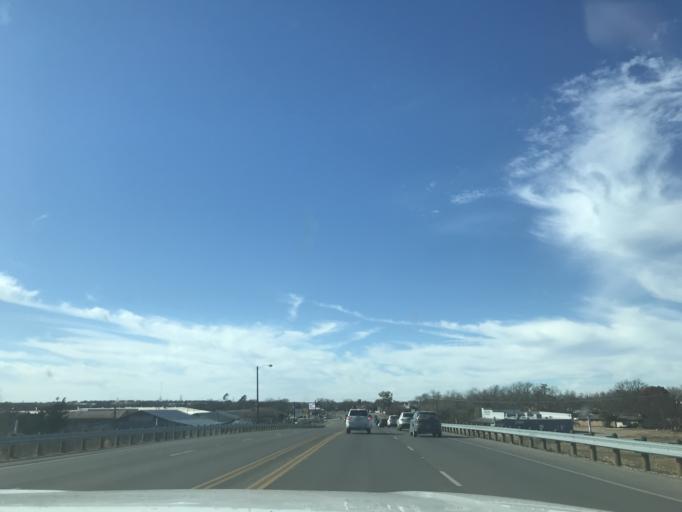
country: US
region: Texas
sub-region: Erath County
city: Stephenville
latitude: 32.2060
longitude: -98.2195
